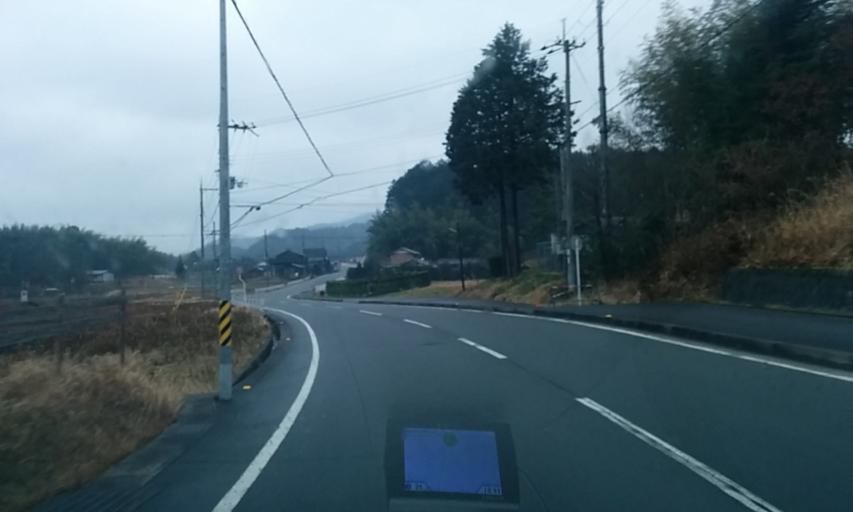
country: JP
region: Kyoto
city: Ayabe
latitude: 35.1720
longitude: 135.3810
